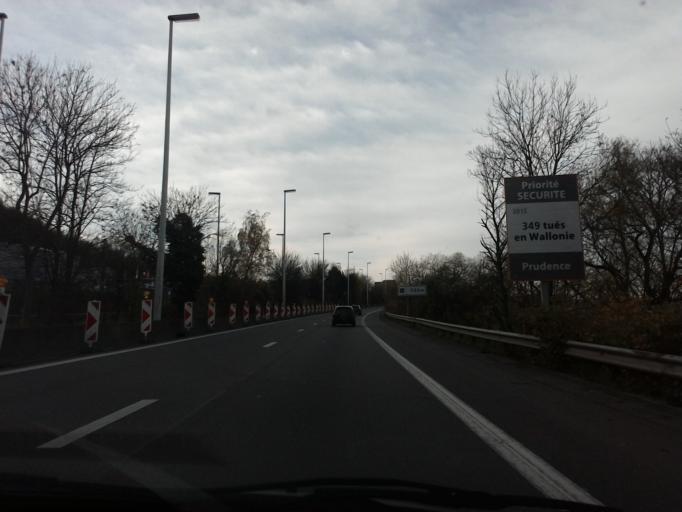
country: BE
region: Wallonia
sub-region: Province de Liege
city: Herstal
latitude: 50.6533
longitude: 5.6434
